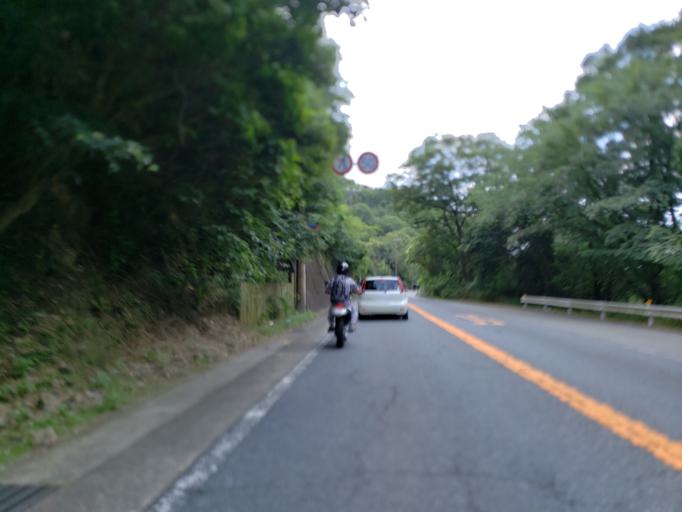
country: JP
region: Hyogo
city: Aioi
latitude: 34.7828
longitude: 134.4379
